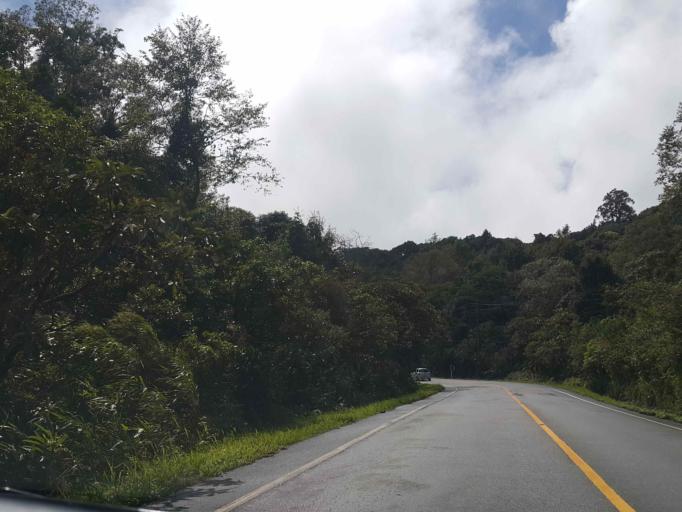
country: TH
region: Chiang Mai
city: Mae Chaem
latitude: 18.5122
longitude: 98.5087
